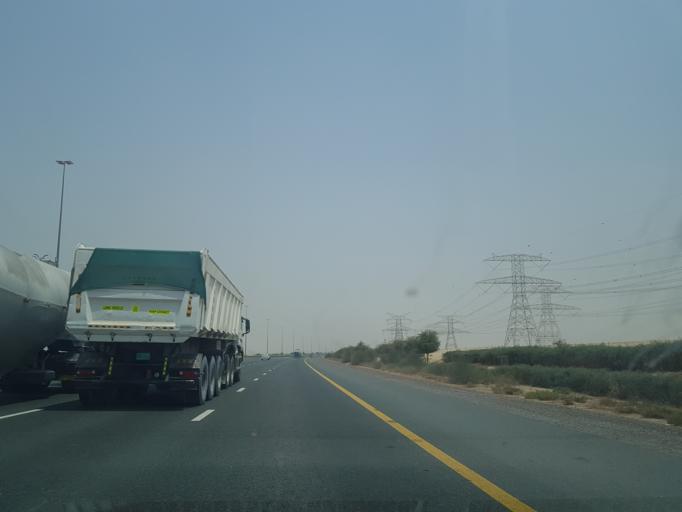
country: AE
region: Dubai
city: Dubai
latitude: 25.0626
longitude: 55.3304
